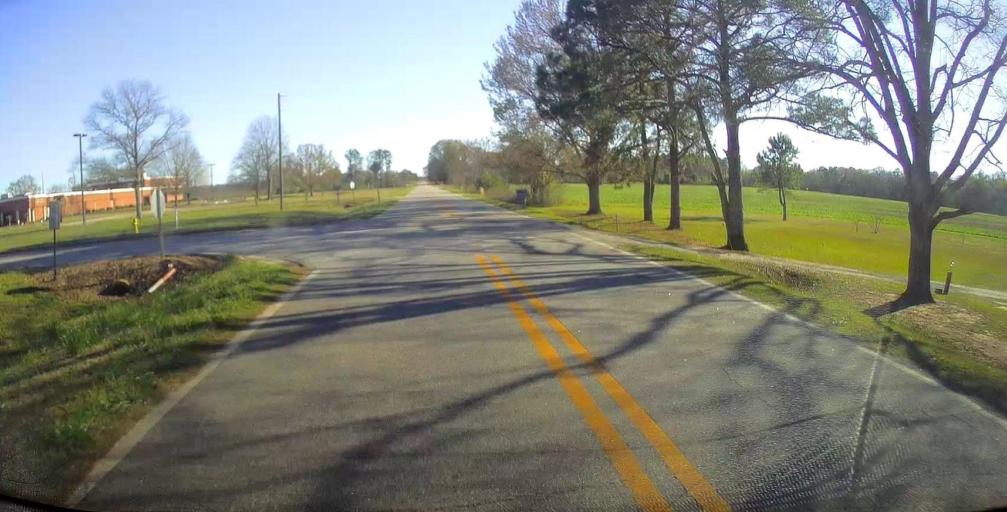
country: US
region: Georgia
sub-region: Peach County
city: Fort Valley
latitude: 32.5704
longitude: -83.9156
